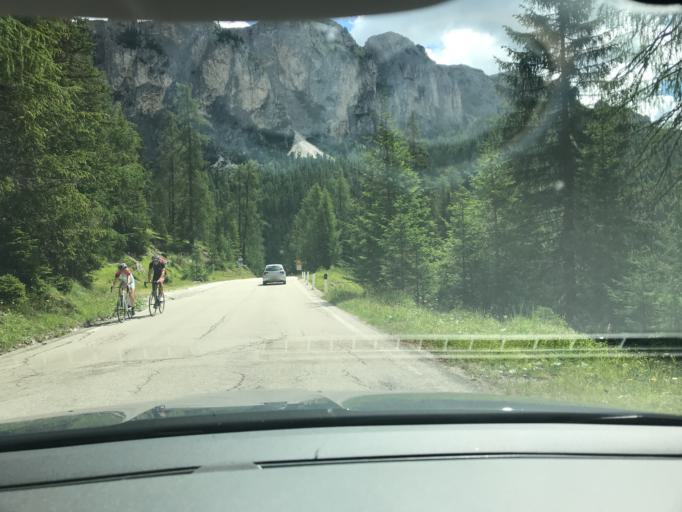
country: IT
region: Veneto
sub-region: Provincia di Belluno
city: Livinallongo del Col di Lana
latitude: 46.5099
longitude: 11.9958
